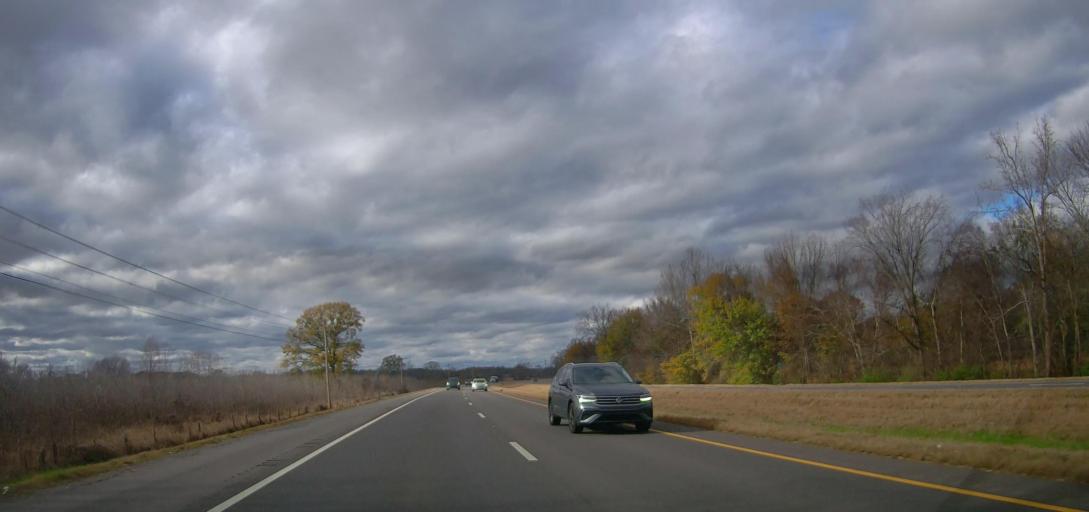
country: US
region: Alabama
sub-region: Lawrence County
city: Moulton
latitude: 34.4669
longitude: -87.2614
